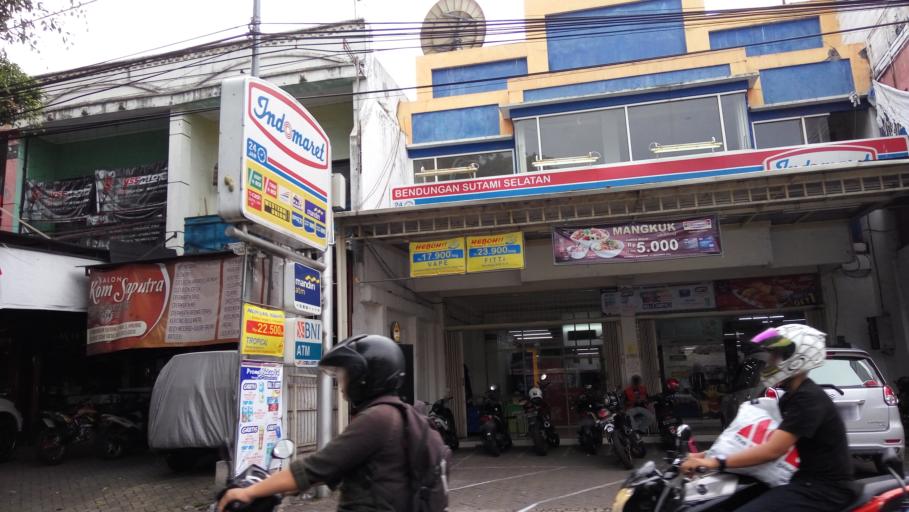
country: ID
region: East Java
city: Malang
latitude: -7.9617
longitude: 112.6135
